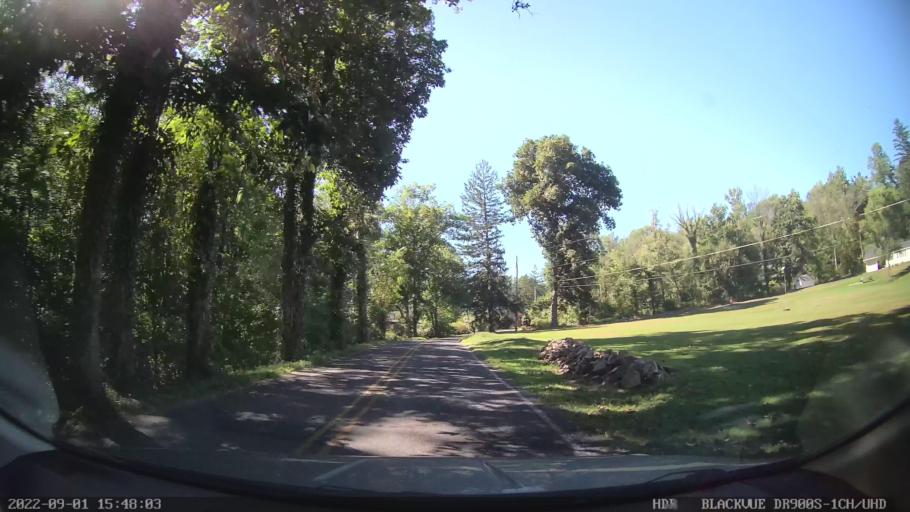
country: US
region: Pennsylvania
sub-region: Berks County
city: Topton
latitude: 40.4716
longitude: -75.7256
